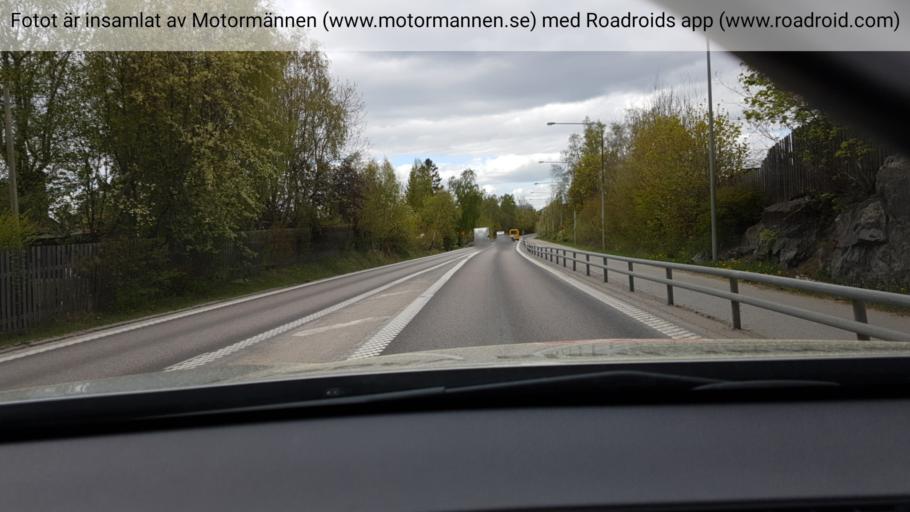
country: SE
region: Stockholm
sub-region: Tyreso Kommun
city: Bollmora
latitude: 59.2148
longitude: 18.2074
